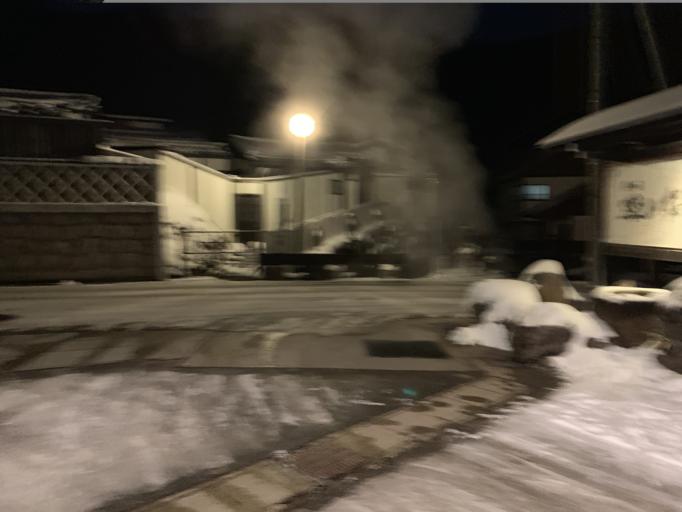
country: JP
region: Gifu
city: Takayama
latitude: 36.1937
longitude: 137.5516
